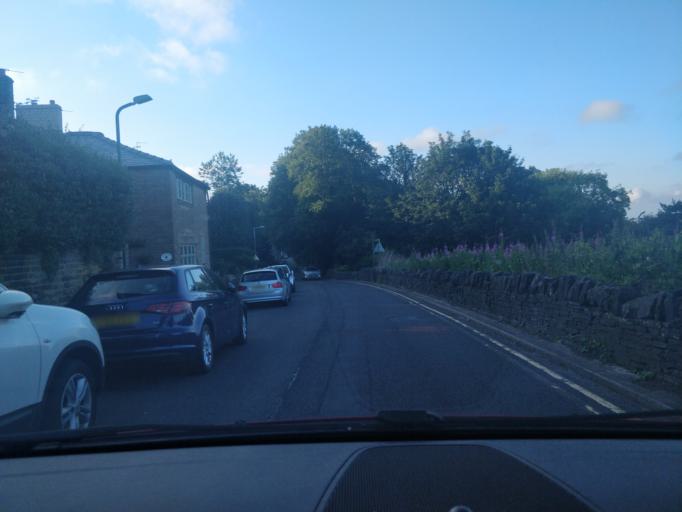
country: GB
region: England
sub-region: Lancashire
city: Appley Bridge
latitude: 53.5386
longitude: -2.7214
